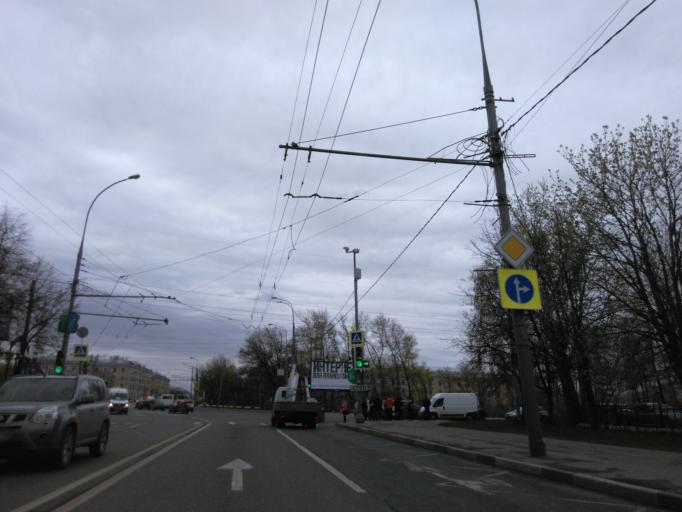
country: RU
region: Moscow
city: Pokrovskoye-Streshnevo
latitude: 55.8369
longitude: 37.4540
